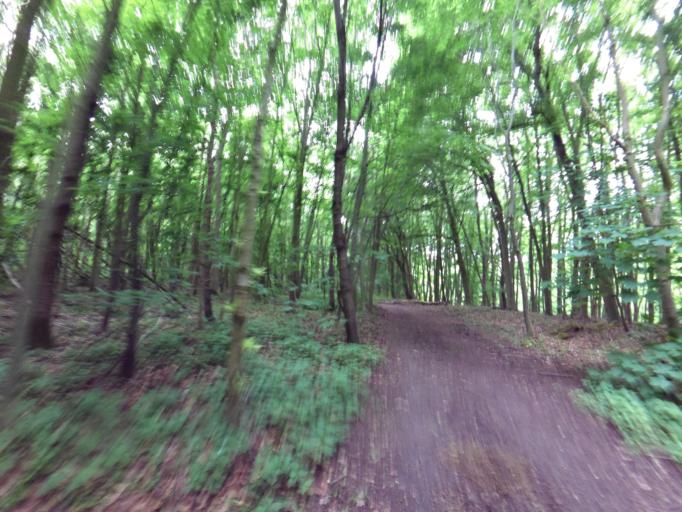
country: NL
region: Limburg
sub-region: Gemeente Kerkrade
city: Kerkrade
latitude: 50.8754
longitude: 6.0313
